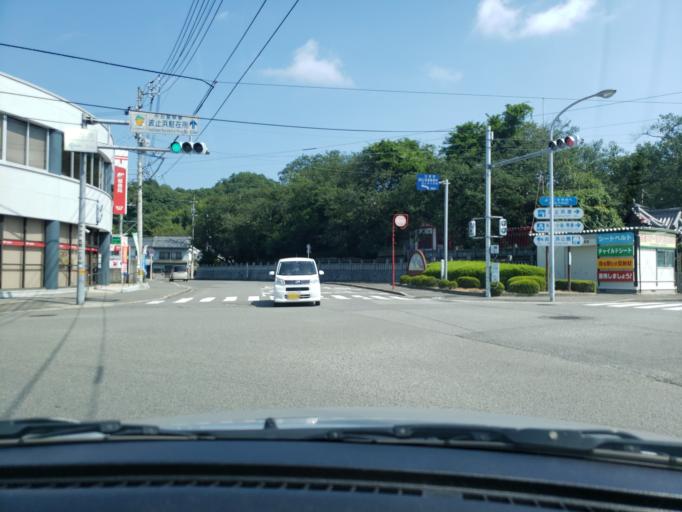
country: JP
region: Ehime
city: Hojo
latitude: 34.1054
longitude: 132.9667
